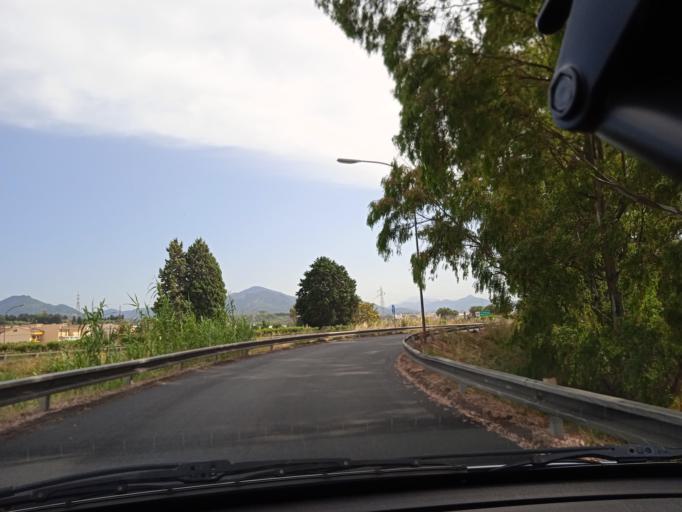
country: IT
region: Sicily
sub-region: Messina
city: San Filippo del Mela
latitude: 38.1930
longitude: 15.2749
